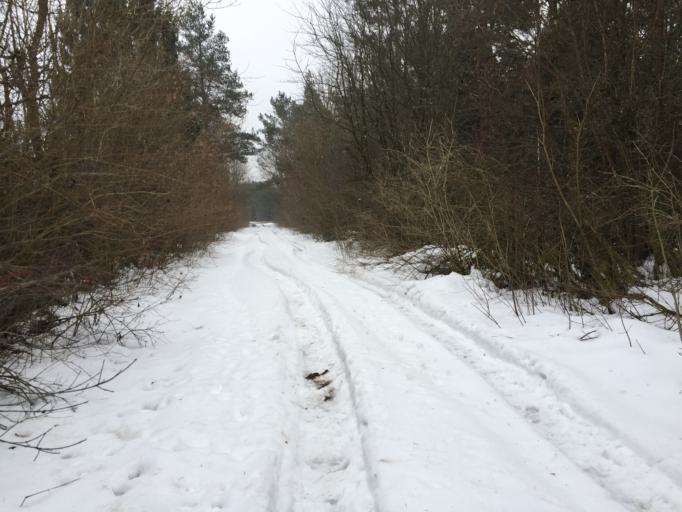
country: EE
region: Saare
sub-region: Orissaare vald
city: Orissaare
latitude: 58.4198
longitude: 22.8202
